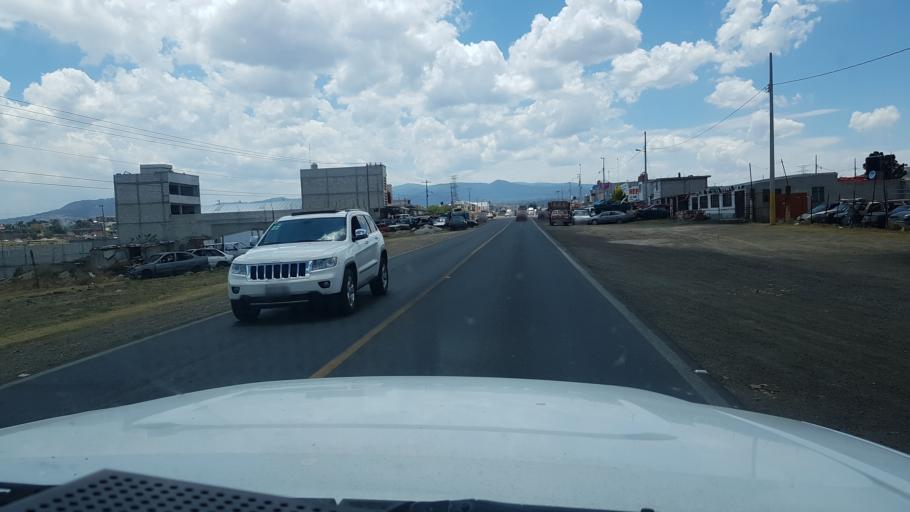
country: MX
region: Hidalgo
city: Calpulalpan
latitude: 19.6004
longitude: -98.5681
